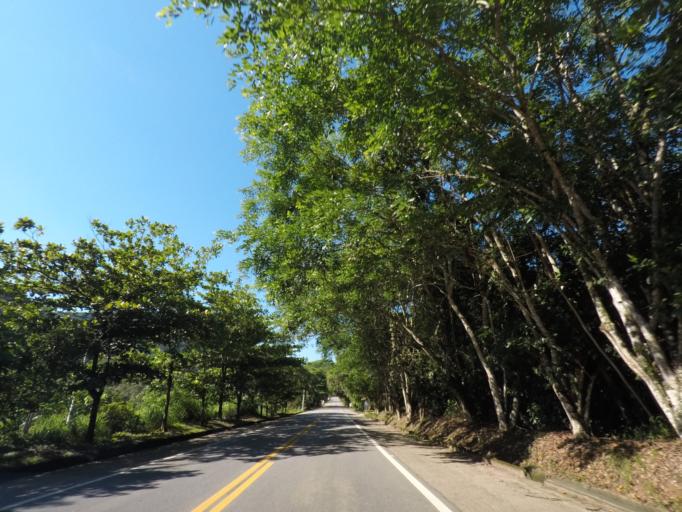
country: BR
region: Rio de Janeiro
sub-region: Parati
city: Paraty
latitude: -23.2772
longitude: -44.6899
